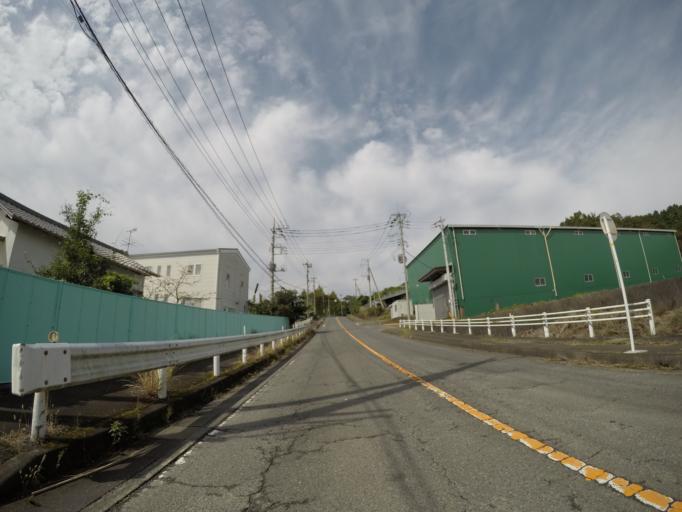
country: JP
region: Shizuoka
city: Fuji
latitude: 35.1935
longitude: 138.6980
